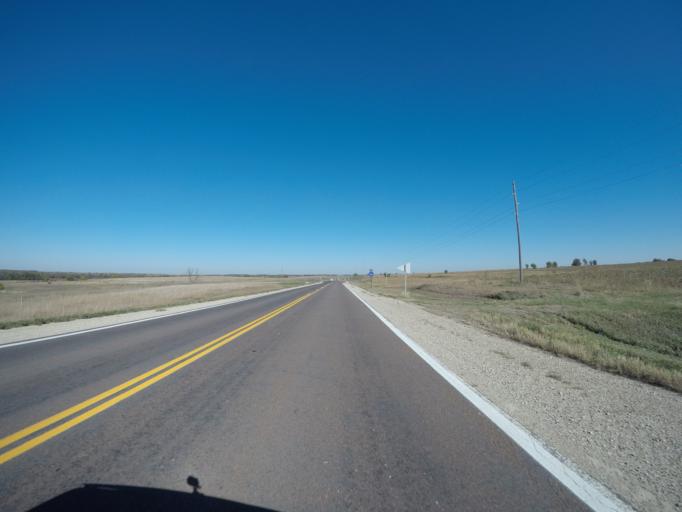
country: US
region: Kansas
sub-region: Clay County
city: Clay Center
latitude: 39.3118
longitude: -96.9236
